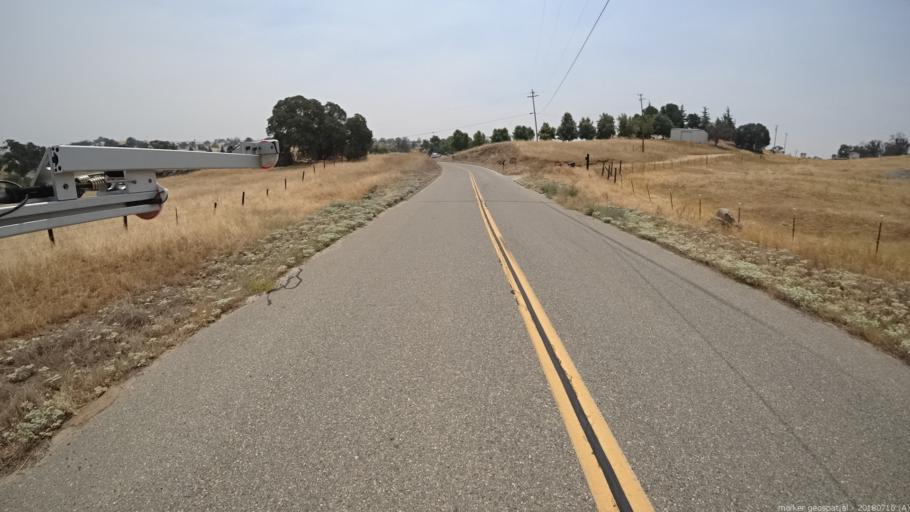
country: US
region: California
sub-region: Madera County
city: Yosemite Lakes
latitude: 37.1354
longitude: -119.9021
